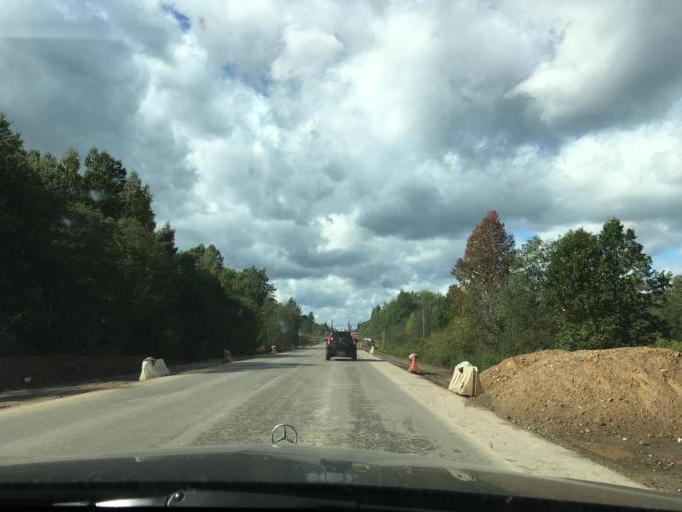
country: RU
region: Pskov
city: Novosokol'niki
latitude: 56.2821
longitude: 30.2902
